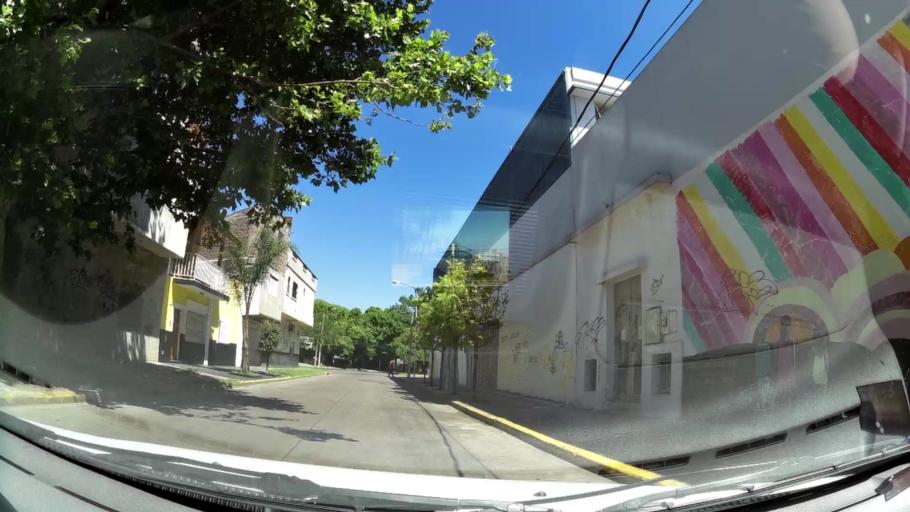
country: AR
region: Buenos Aires
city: Caseros
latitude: -34.6021
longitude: -58.5497
